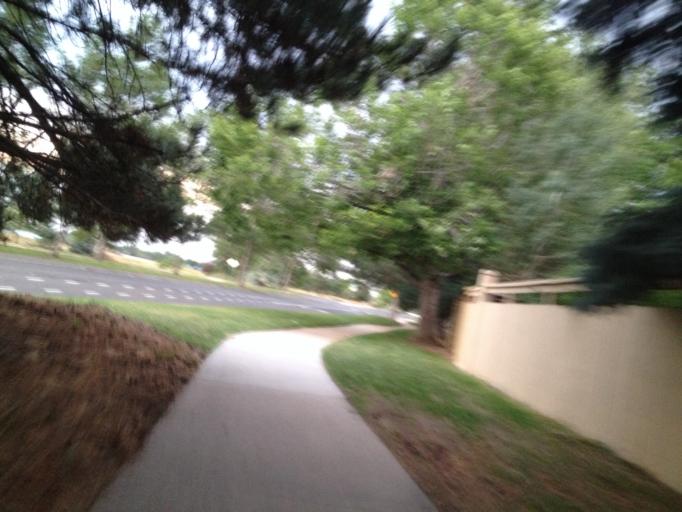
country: US
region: Colorado
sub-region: Boulder County
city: Louisville
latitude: 39.9650
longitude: -105.1500
